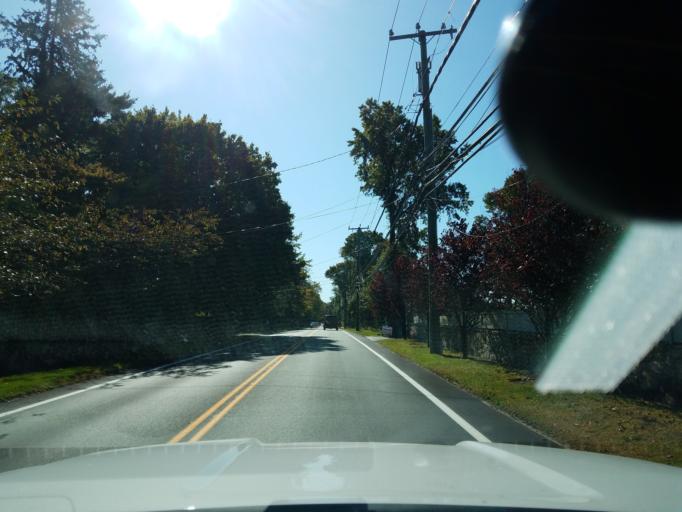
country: US
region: Connecticut
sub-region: Fairfield County
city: Cos Cob
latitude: 41.0673
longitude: -73.6211
